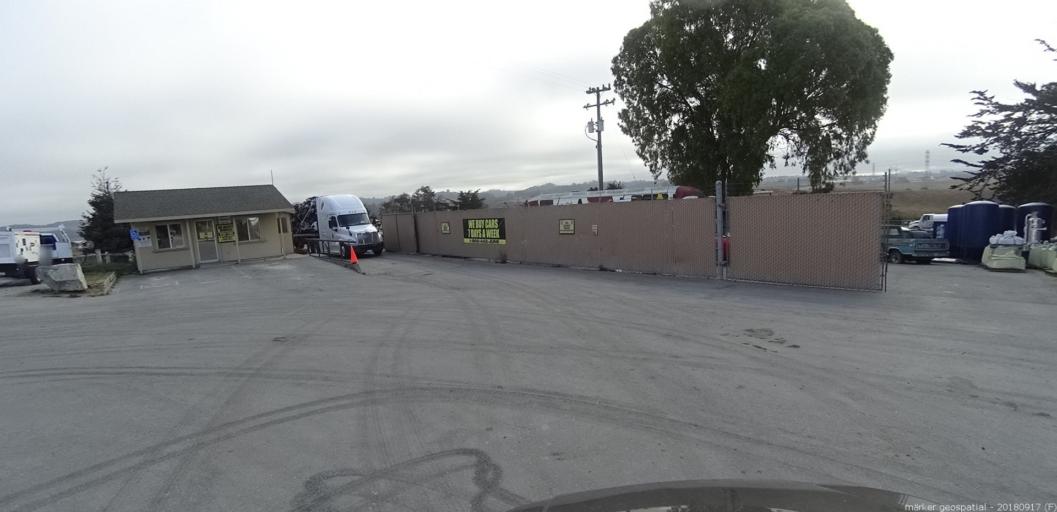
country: US
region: California
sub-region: Monterey County
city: Elkhorn
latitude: 36.8042
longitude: -121.7503
